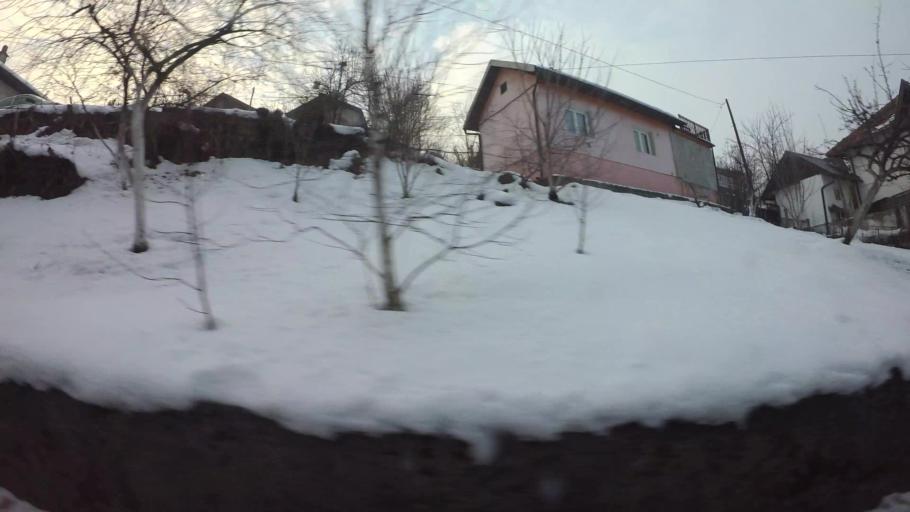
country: BA
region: Federation of Bosnia and Herzegovina
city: Hotonj
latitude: 43.8939
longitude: 18.3708
